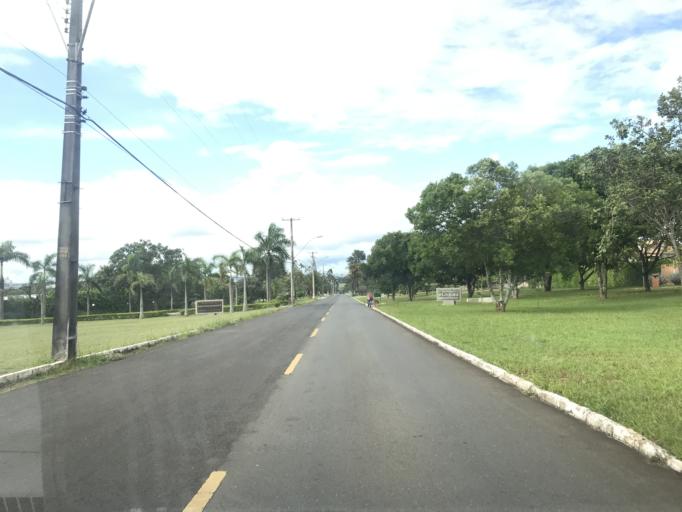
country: BR
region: Federal District
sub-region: Brasilia
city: Brasilia
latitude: -15.8971
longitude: -47.9197
